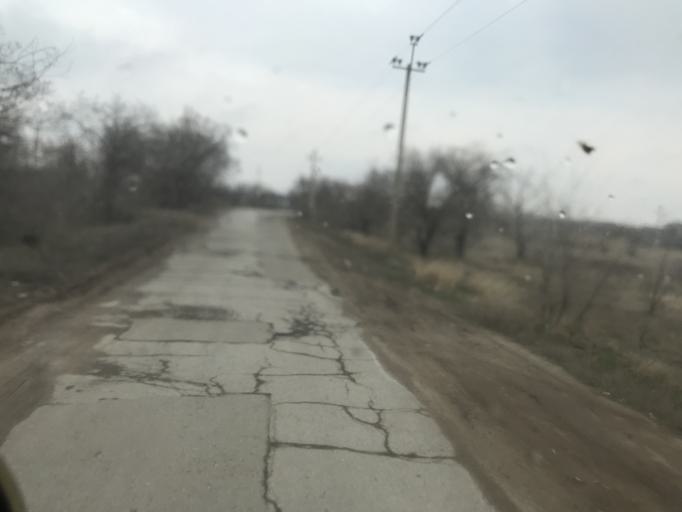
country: RU
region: Volgograd
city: Krasnoslobodsk
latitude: 48.5332
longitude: 44.6066
